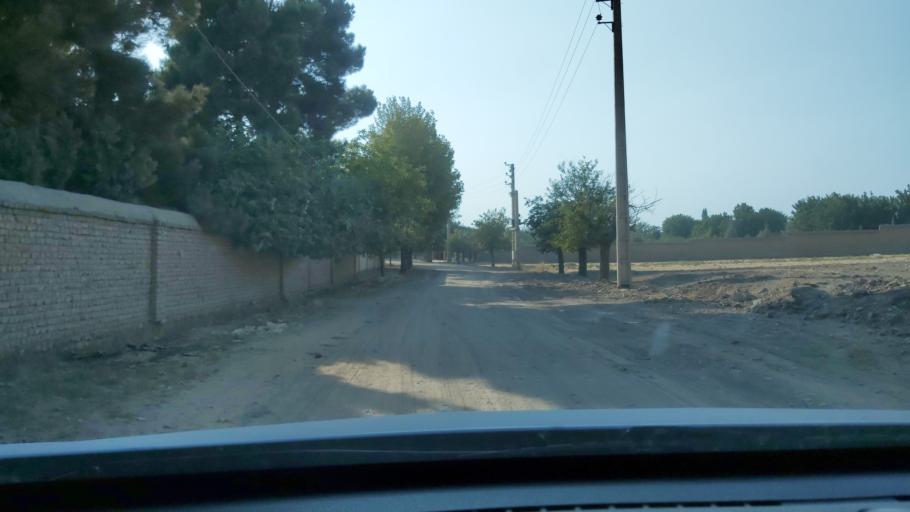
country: IR
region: Alborz
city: Hashtgerd
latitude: 35.9546
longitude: 50.7842
